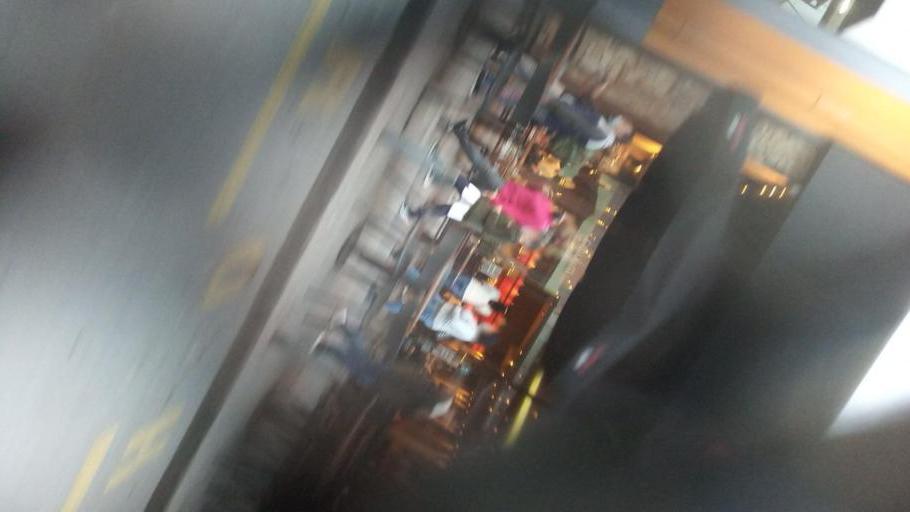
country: AR
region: Jujuy
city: San Salvador de Jujuy
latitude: -24.1855
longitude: -65.3065
